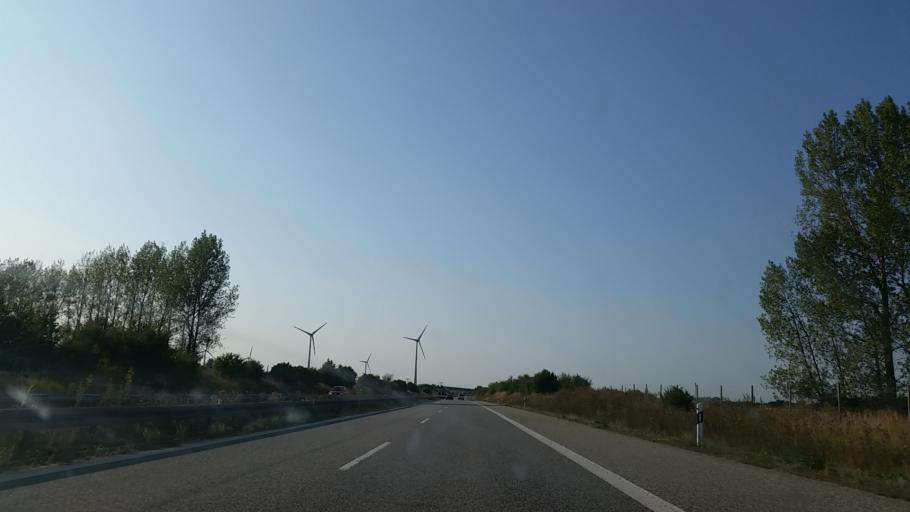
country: DE
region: Brandenburg
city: Schonfeld
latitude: 53.4474
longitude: 13.9844
